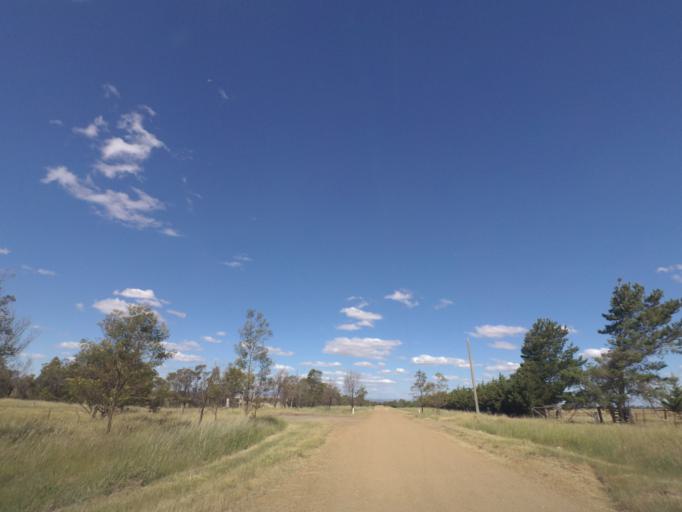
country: AU
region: Victoria
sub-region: Hume
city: Sunbury
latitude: -37.4612
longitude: 144.8115
